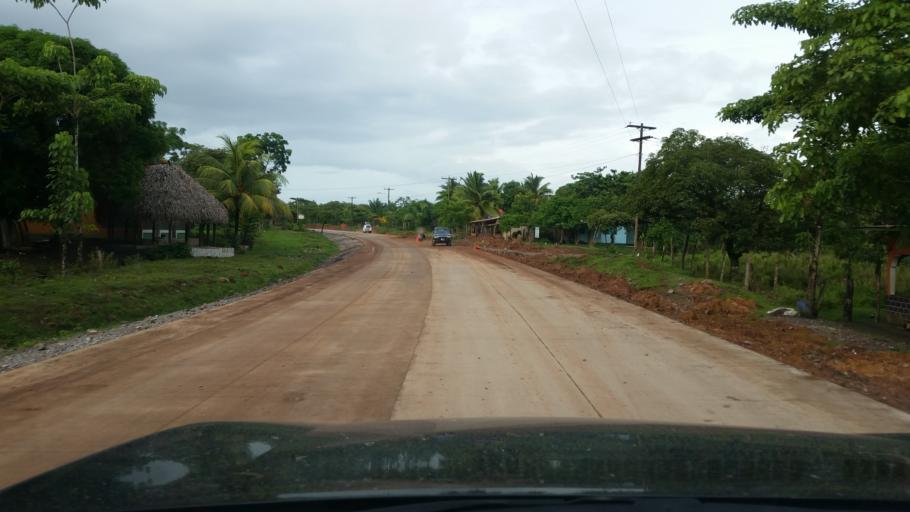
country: NI
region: Matagalpa
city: Rio Blanco
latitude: 13.1206
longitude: -85.0559
